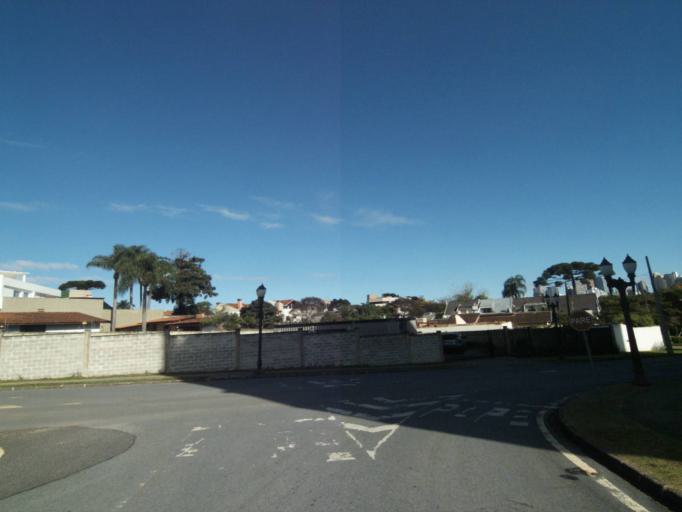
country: BR
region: Parana
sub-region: Curitiba
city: Curitiba
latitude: -25.4129
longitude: -49.2422
